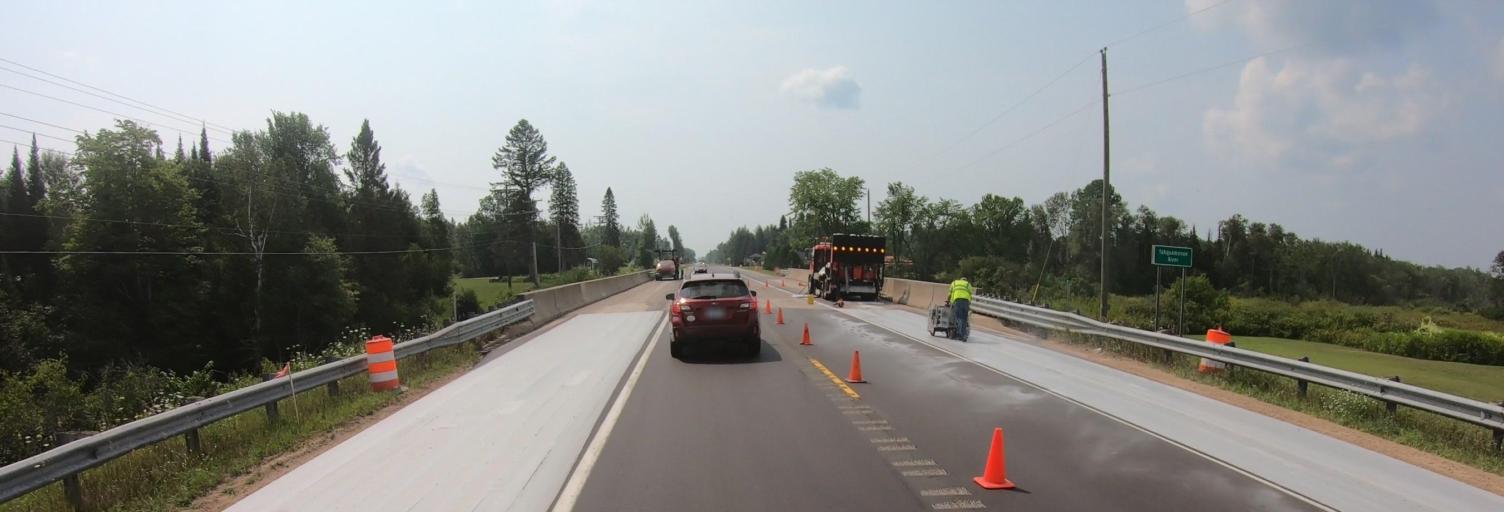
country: US
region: Michigan
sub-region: Luce County
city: Newberry
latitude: 46.3722
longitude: -85.5099
